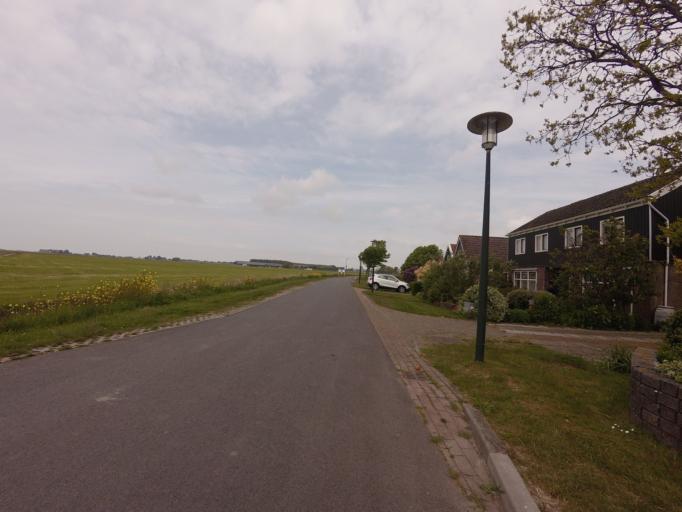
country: NL
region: Friesland
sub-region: Sudwest Fryslan
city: Bolsward
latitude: 53.0842
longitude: 5.4827
